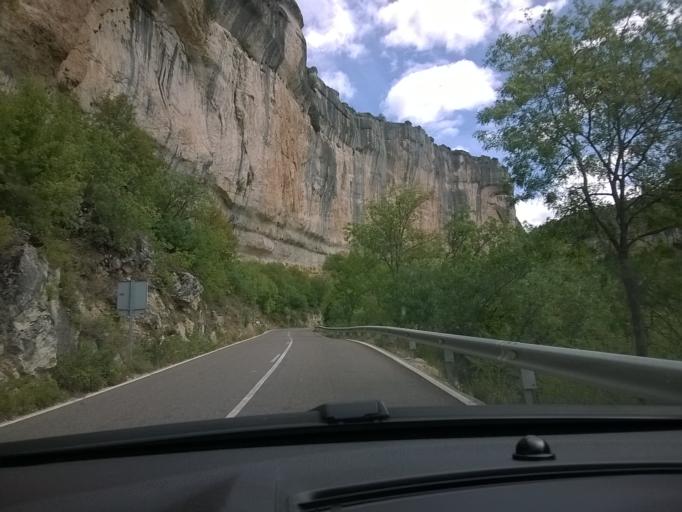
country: ES
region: Castille-La Mancha
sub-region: Provincia de Cuenca
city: Carrascosa
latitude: 40.5431
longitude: -2.1371
